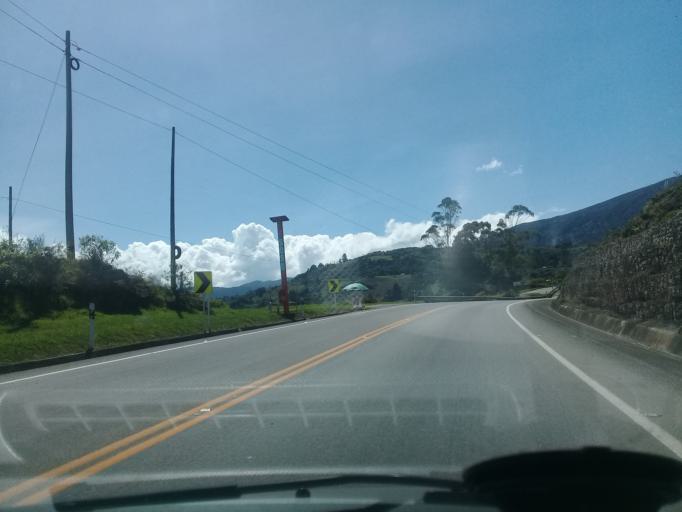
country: CO
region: Cundinamarca
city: Chipaque
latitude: 4.4519
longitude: -74.0557
